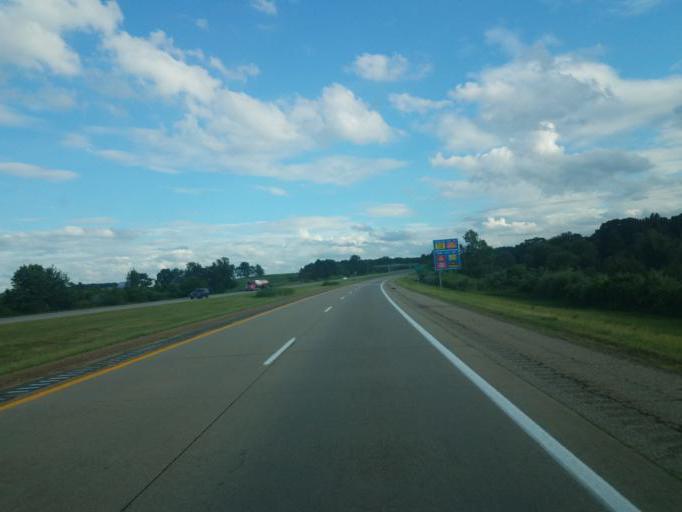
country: US
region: Indiana
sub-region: Steuben County
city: Fremont
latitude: 41.7707
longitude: -84.9879
